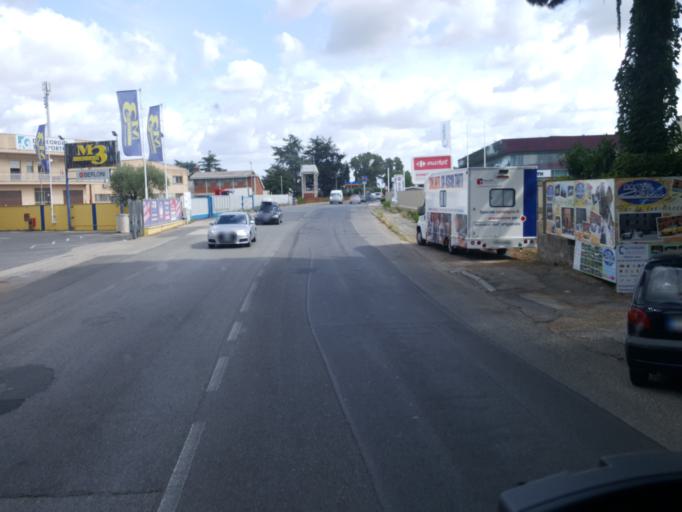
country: IT
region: Latium
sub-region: Citta metropolitana di Roma Capitale
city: Area Produttiva
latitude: 41.6856
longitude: 12.5121
